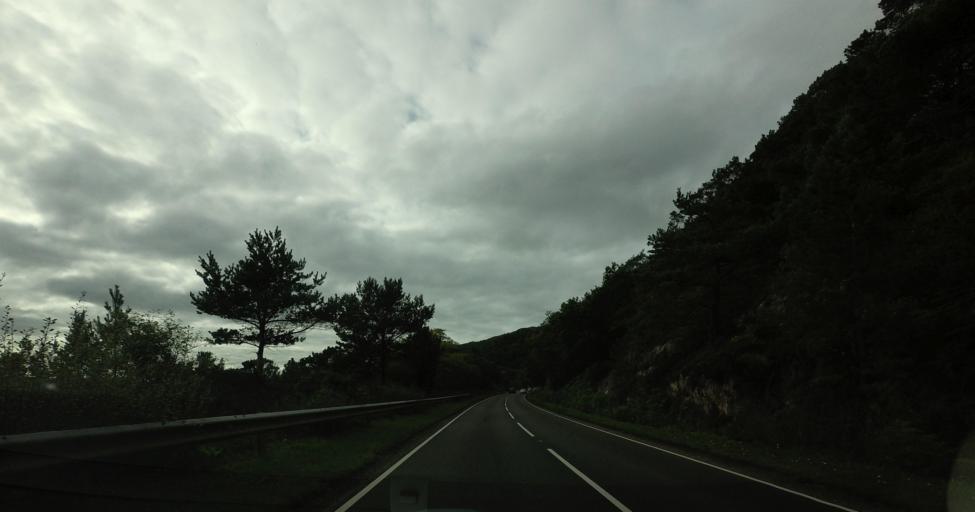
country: GB
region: Scotland
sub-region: Highland
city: Portree
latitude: 57.2803
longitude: -5.6831
